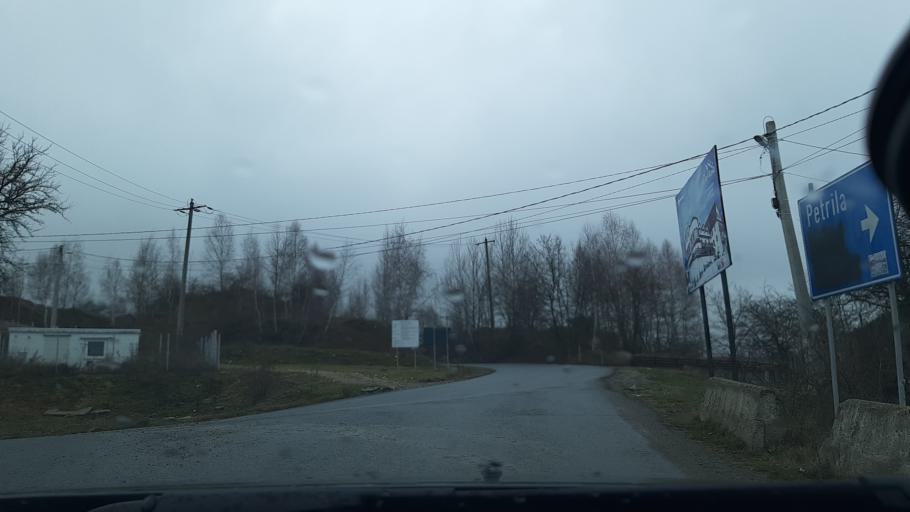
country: RO
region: Hunedoara
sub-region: Oras Petrila
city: Petrila
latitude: 45.4213
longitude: 23.4258
